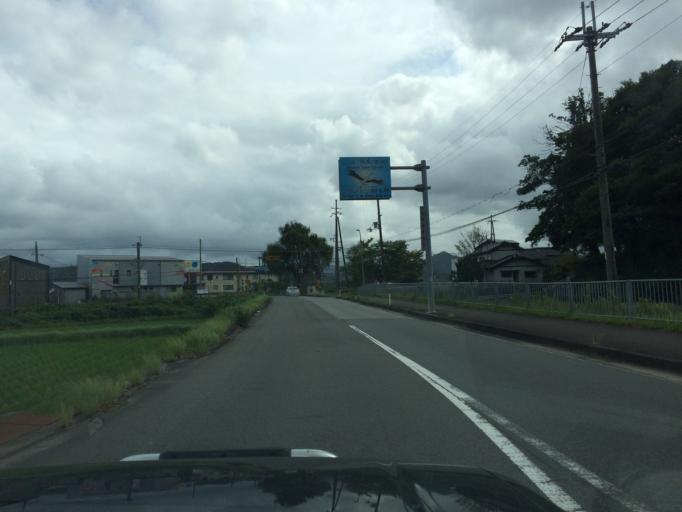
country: JP
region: Hyogo
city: Toyooka
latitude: 35.5081
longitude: 134.8114
